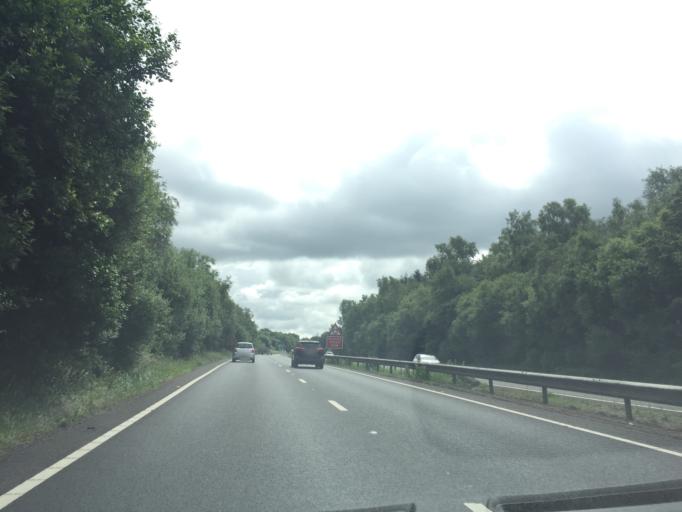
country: GB
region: England
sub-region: Dorset
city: Ferndown
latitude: 50.8148
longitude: -1.8803
